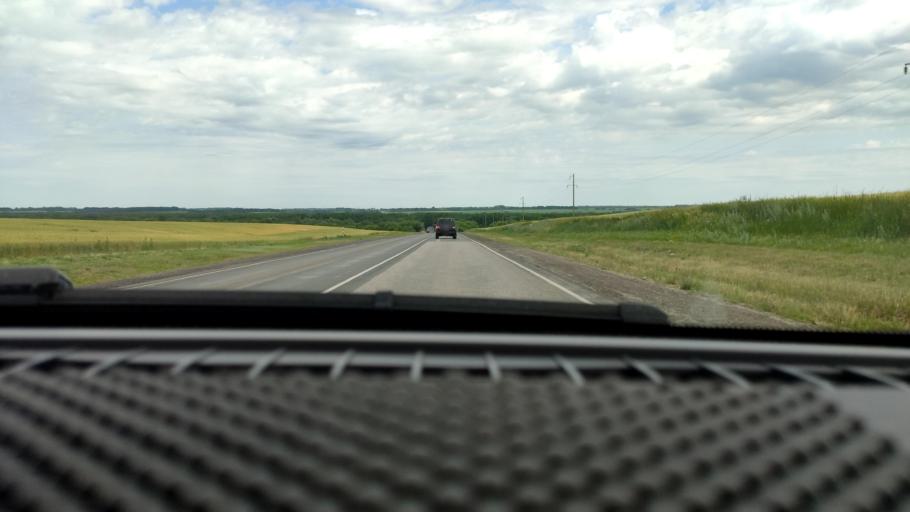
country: RU
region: Voronezj
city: Orlovo
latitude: 51.6823
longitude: 39.5646
